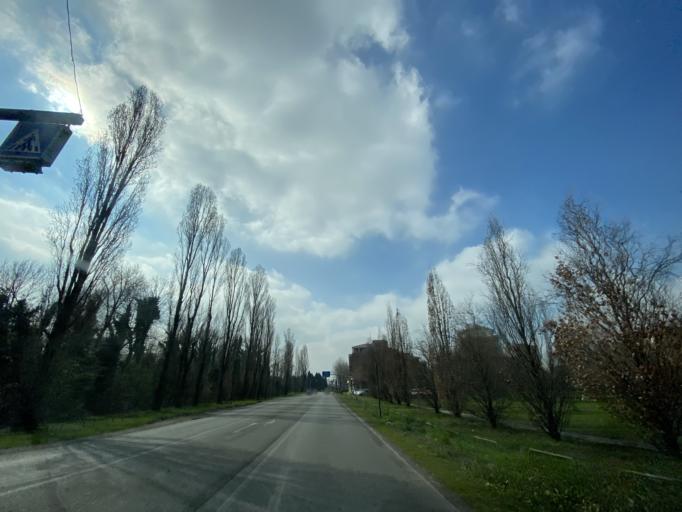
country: IT
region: Lombardy
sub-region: Citta metropolitana di Milano
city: Bresso
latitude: 45.5367
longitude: 9.1799
